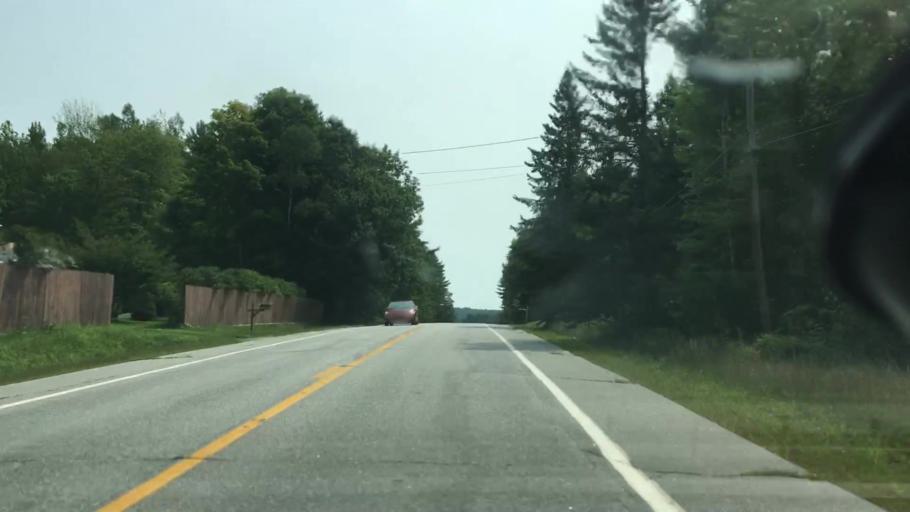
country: US
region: Maine
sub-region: Kennebec County
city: Wayne
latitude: 44.3988
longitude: -70.1223
